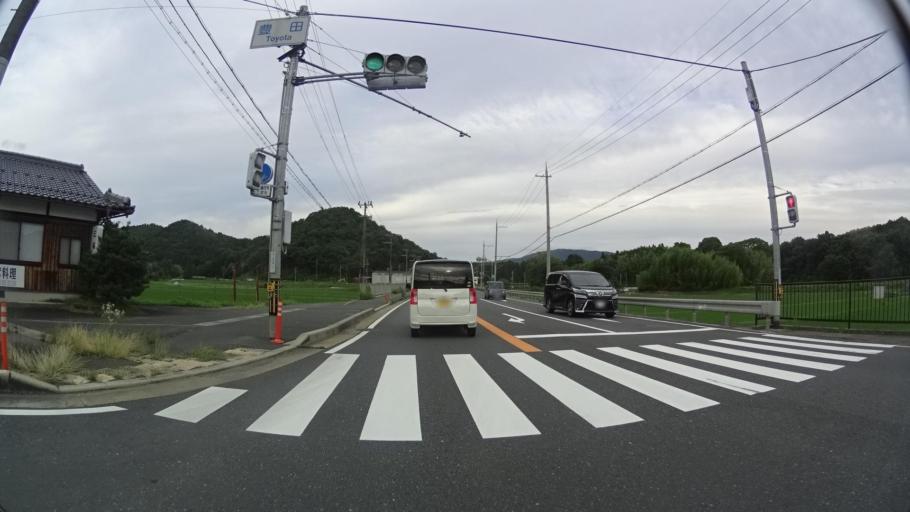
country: JP
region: Kyoto
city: Ayabe
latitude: 35.1753
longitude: 135.4054
